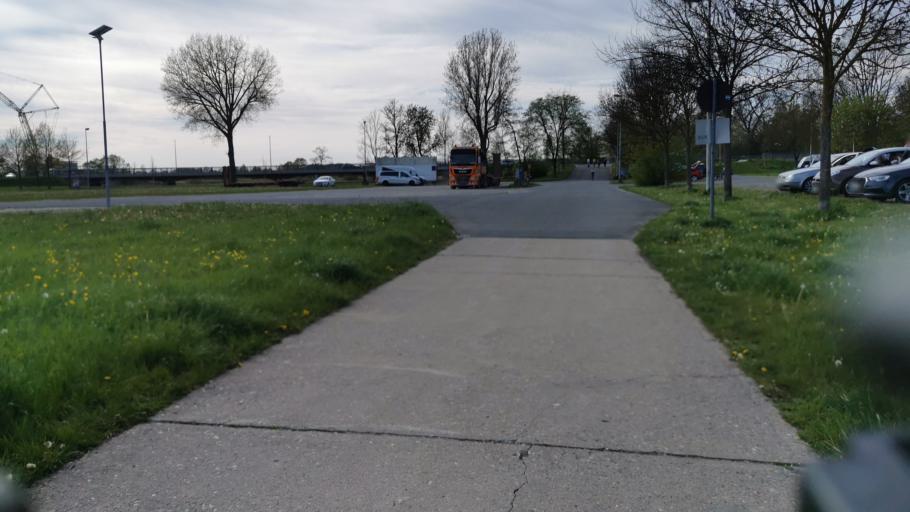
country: DE
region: Bavaria
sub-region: Regierungsbezirk Mittelfranken
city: Hochstadt an der Aisch
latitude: 49.6996
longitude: 10.8063
